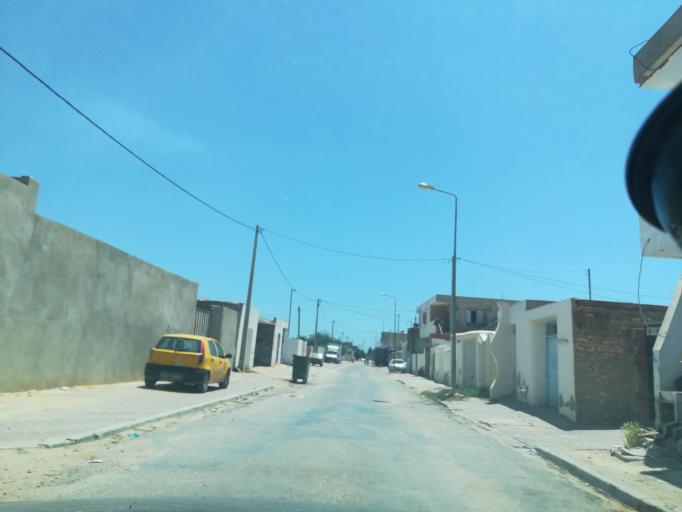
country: TN
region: Safaqis
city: Al Qarmadah
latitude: 34.8244
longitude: 10.7539
